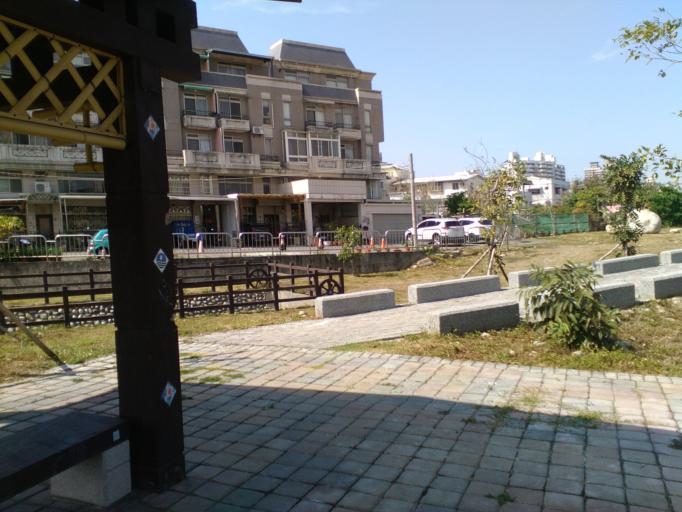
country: TW
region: Taiwan
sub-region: Taichung City
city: Taichung
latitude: 24.1113
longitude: 120.6722
